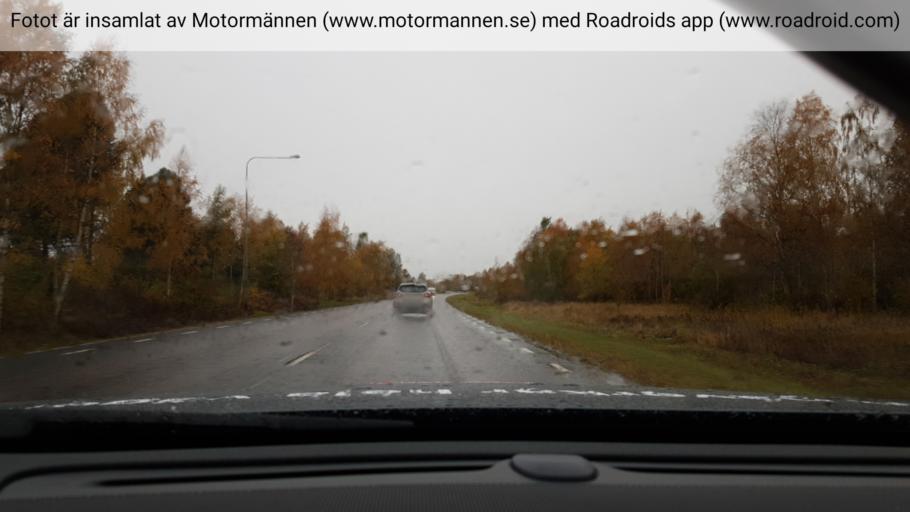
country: SE
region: Norrbotten
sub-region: Lulea Kommun
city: Sodra Sunderbyn
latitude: 65.6568
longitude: 21.9632
